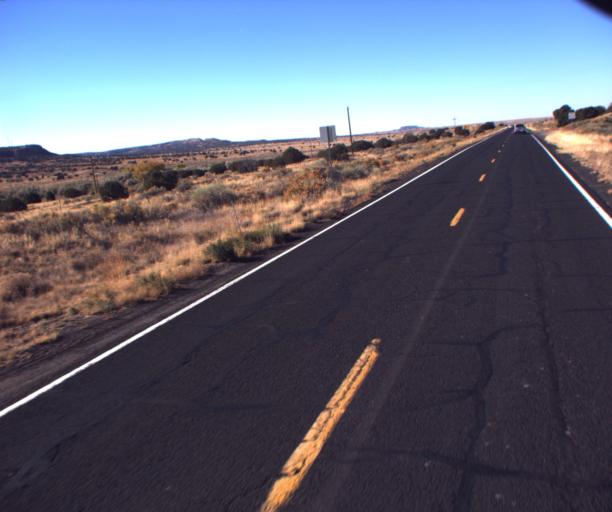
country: US
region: Arizona
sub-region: Navajo County
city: First Mesa
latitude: 35.8337
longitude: -110.2681
